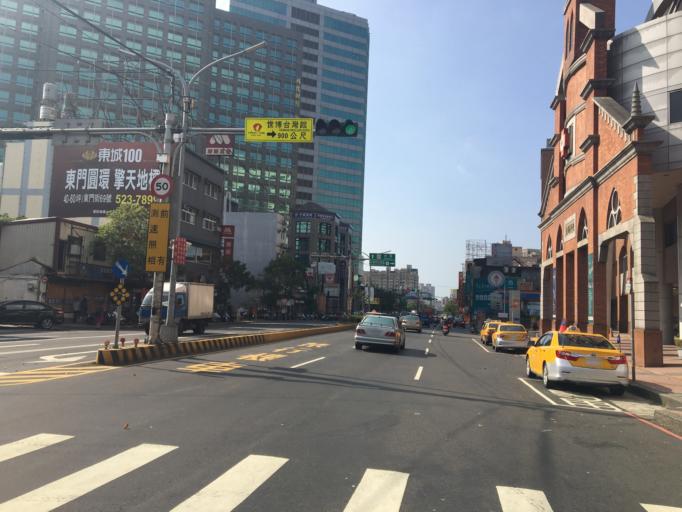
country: TW
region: Taiwan
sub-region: Hsinchu
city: Hsinchu
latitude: 24.7999
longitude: 120.9910
